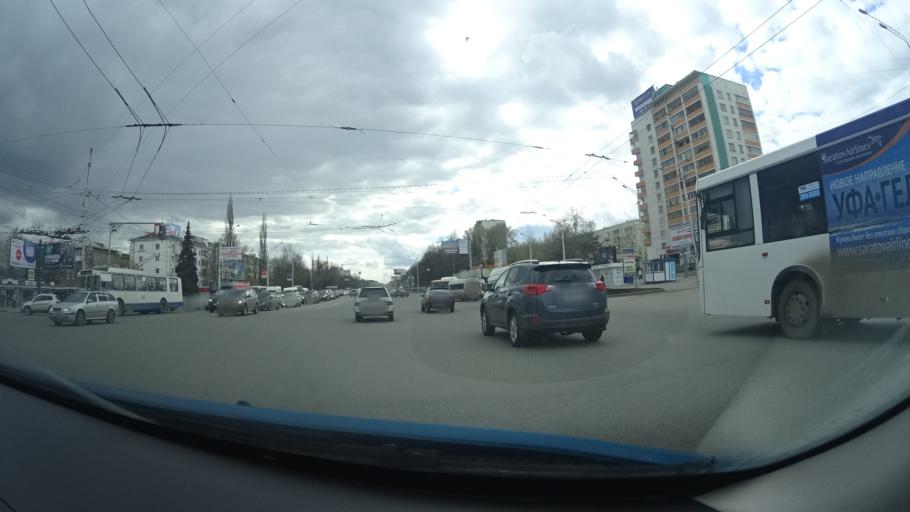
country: RU
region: Bashkortostan
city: Ufa
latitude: 54.7560
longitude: 56.0053
